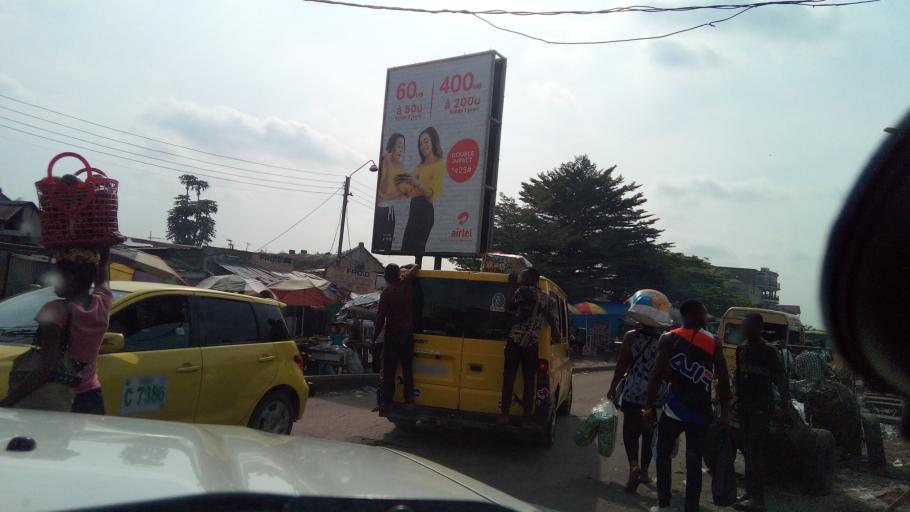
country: CD
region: Kinshasa
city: Kinshasa
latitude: -4.3469
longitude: 15.3119
